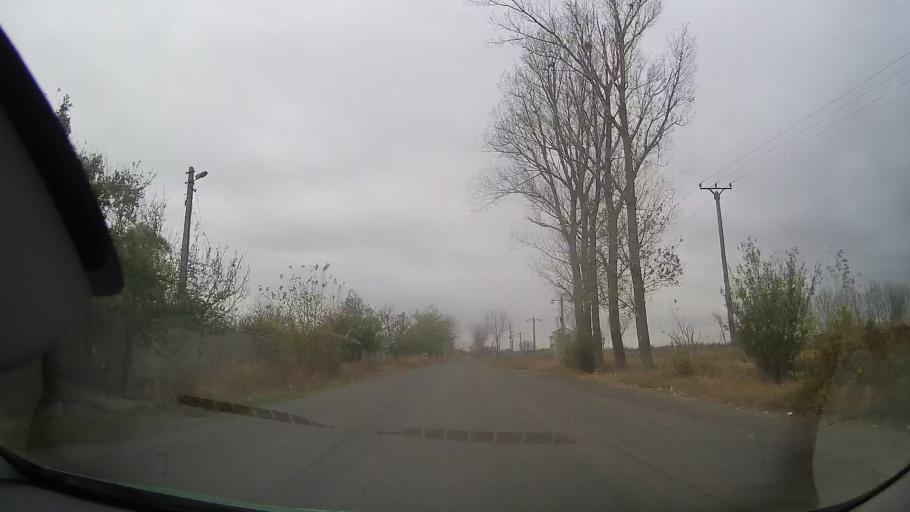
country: RO
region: Braila
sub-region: Comuna Ciresu
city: Ciresu
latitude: 44.9396
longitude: 27.3764
